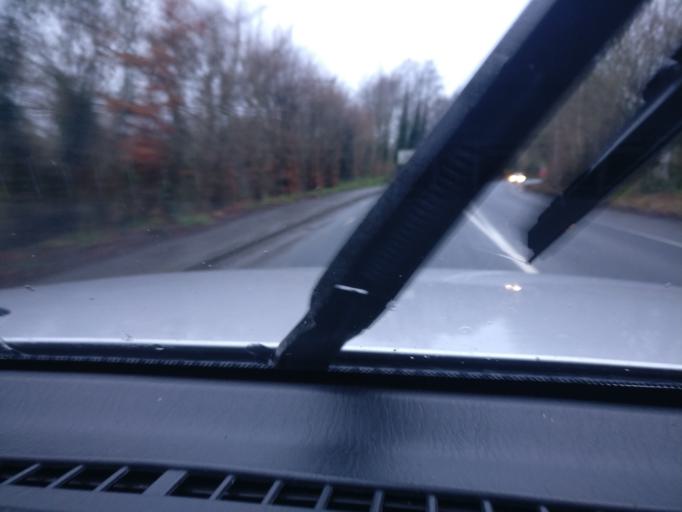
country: IE
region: Leinster
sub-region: An Mhi
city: Trim
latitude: 53.5476
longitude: -6.7903
